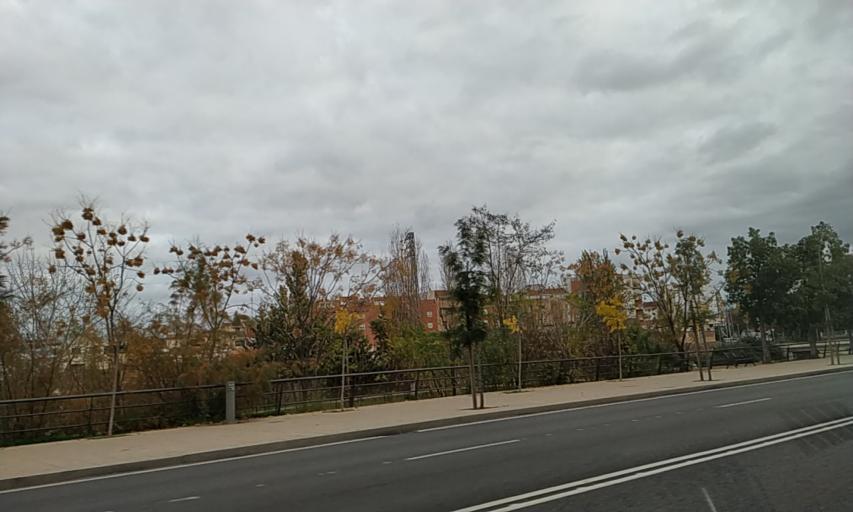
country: ES
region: Extremadura
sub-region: Provincia de Badajoz
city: Badajoz
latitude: 38.8806
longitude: -6.9640
